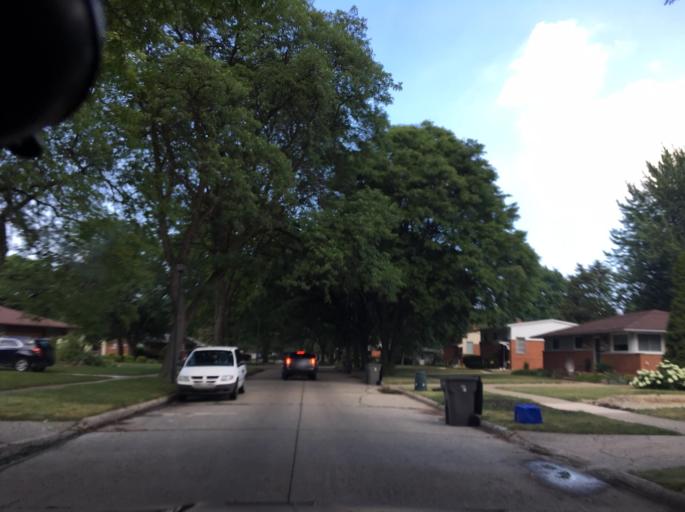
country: US
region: Michigan
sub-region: Macomb County
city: Clinton
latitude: 42.5641
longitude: -82.9085
